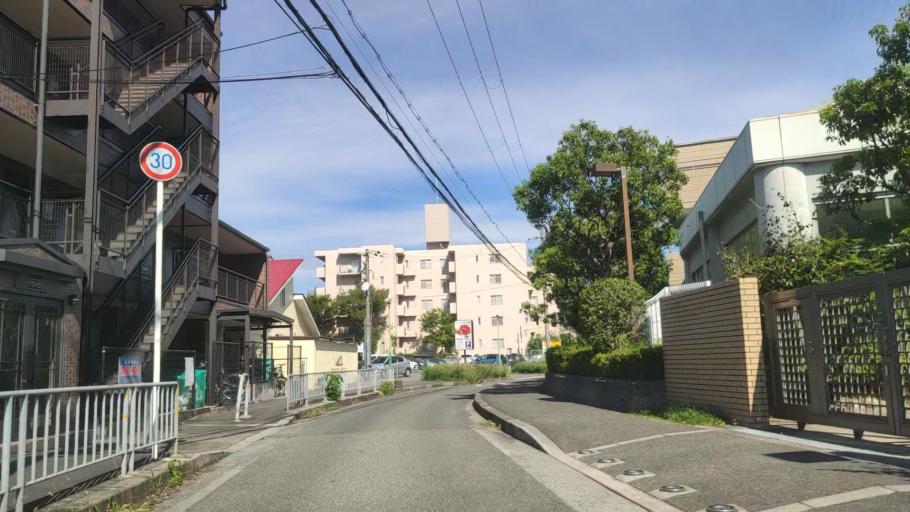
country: JP
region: Osaka
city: Suita
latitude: 34.8105
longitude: 135.5170
